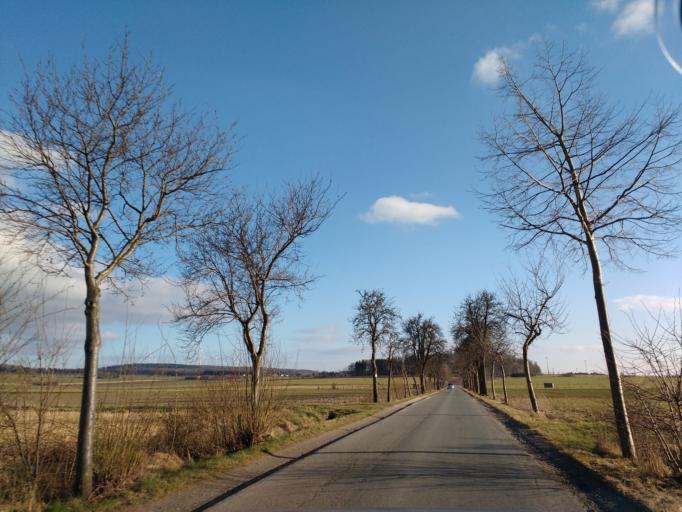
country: DE
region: North Rhine-Westphalia
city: Bad Lippspringe
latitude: 51.7643
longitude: 8.8400
